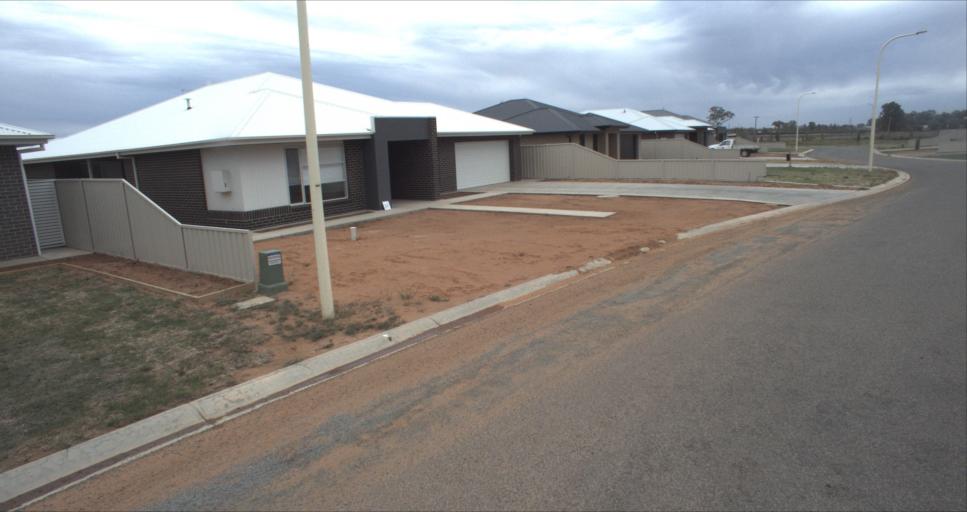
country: AU
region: New South Wales
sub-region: Leeton
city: Leeton
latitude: -34.5401
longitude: 146.3996
